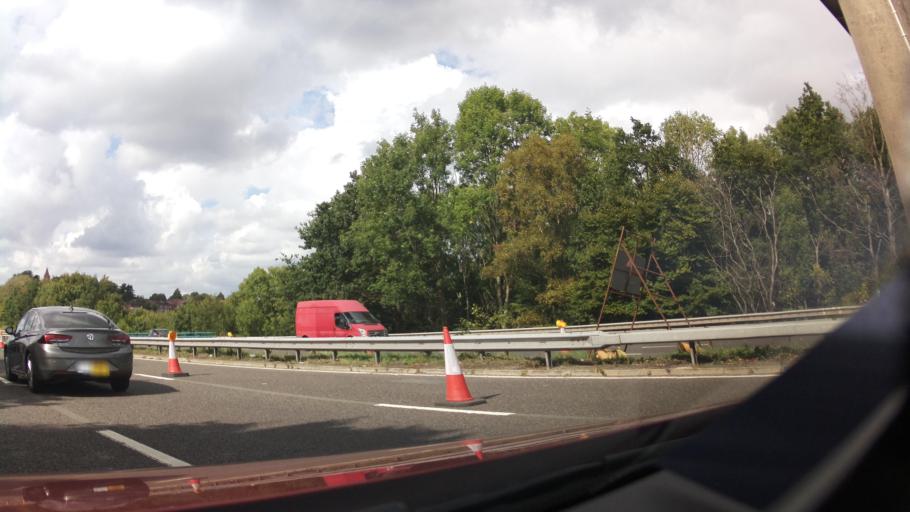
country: GB
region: England
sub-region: Borough of Tameside
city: Hyde
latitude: 53.4567
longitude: -2.0931
